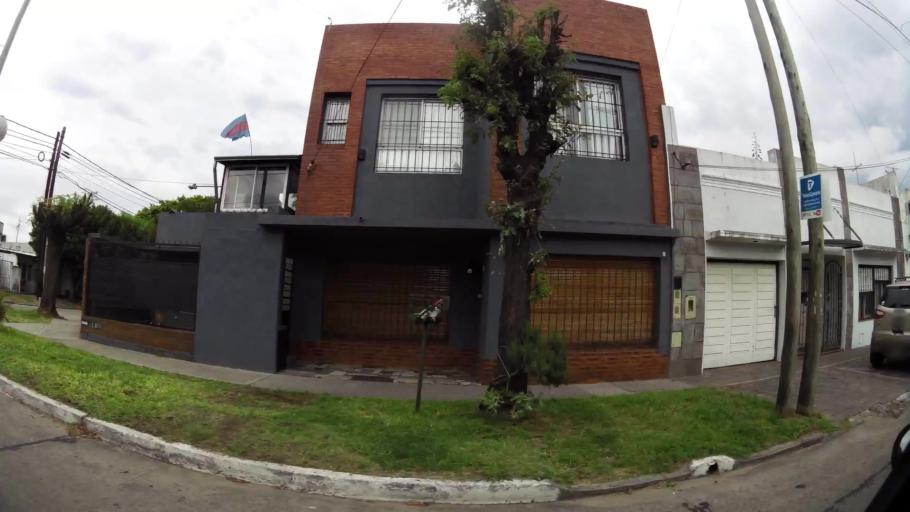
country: AR
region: Buenos Aires
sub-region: Partido de Quilmes
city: Quilmes
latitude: -34.7425
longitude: -58.2859
